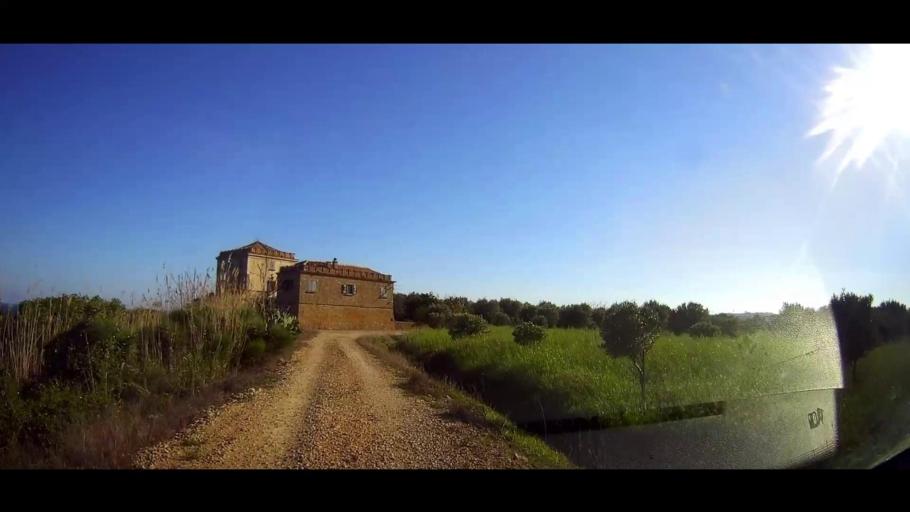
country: IT
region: Calabria
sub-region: Provincia di Crotone
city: Crotone
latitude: 39.0190
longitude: 17.1872
